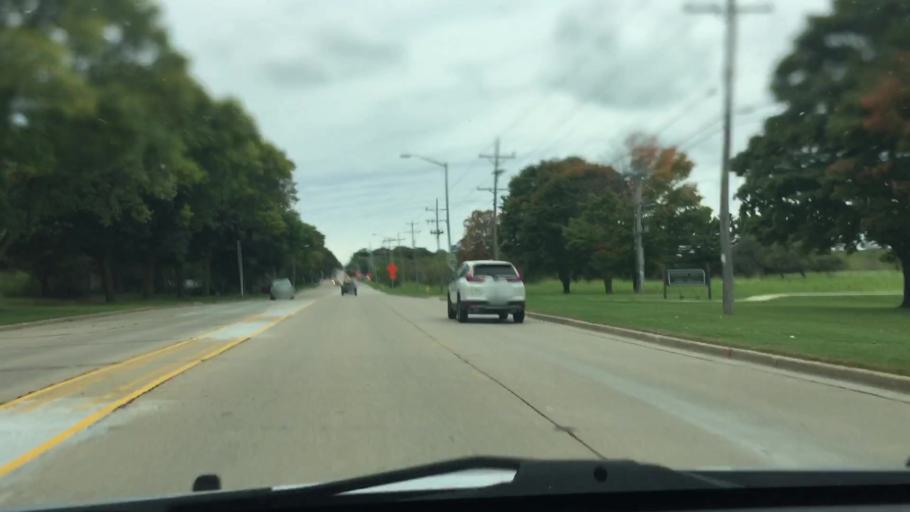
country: US
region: Wisconsin
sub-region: Waukesha County
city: Waukesha
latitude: 43.0323
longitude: -88.2483
